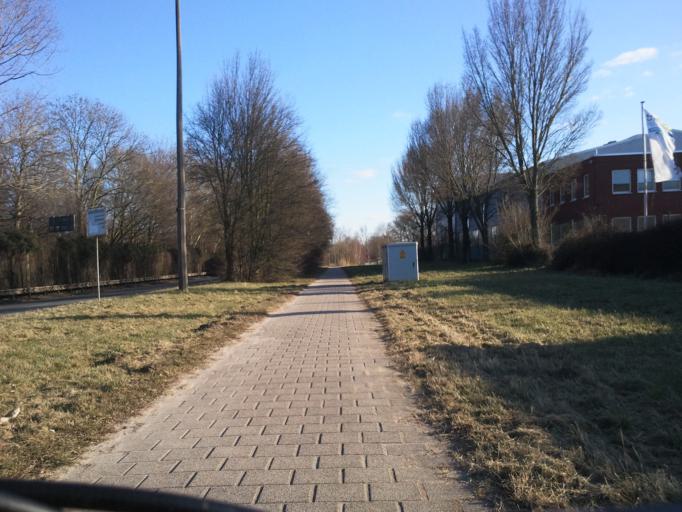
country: DE
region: Lower Saxony
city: Stuhr
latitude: 53.0782
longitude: 8.7583
